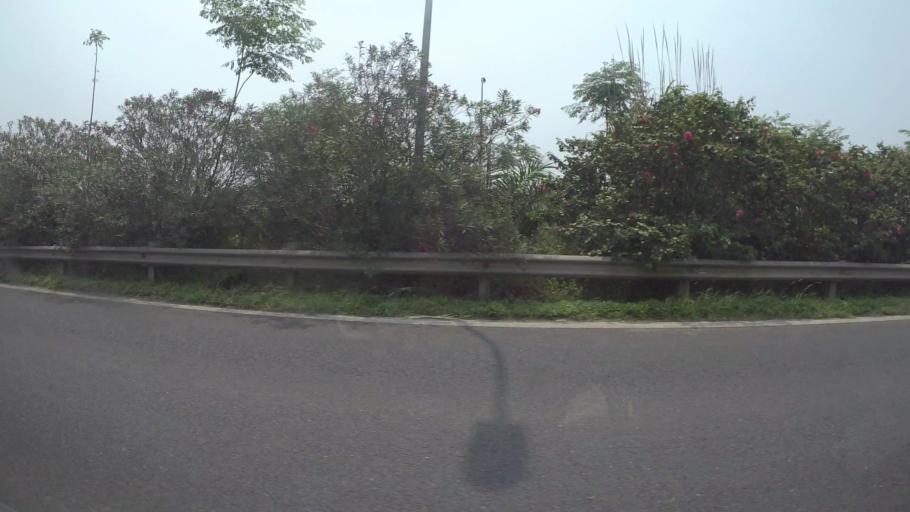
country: VN
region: Ha Noi
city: Quoc Oai
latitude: 20.9960
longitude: 105.5910
